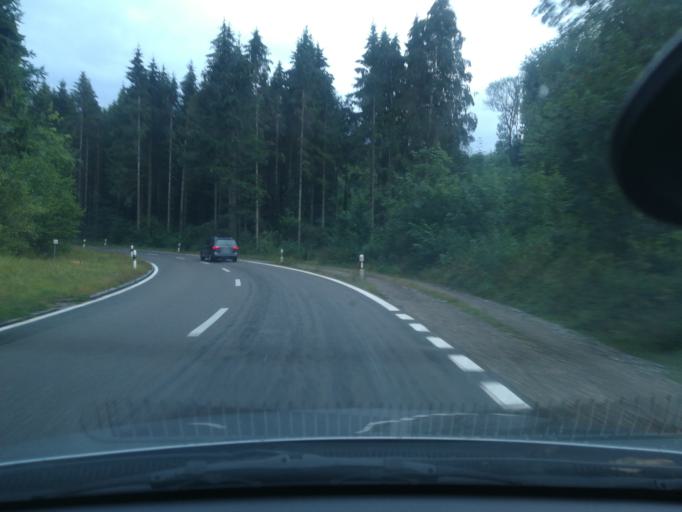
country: CH
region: Thurgau
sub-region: Frauenfeld District
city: Huttwilen
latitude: 47.6217
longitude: 8.8808
